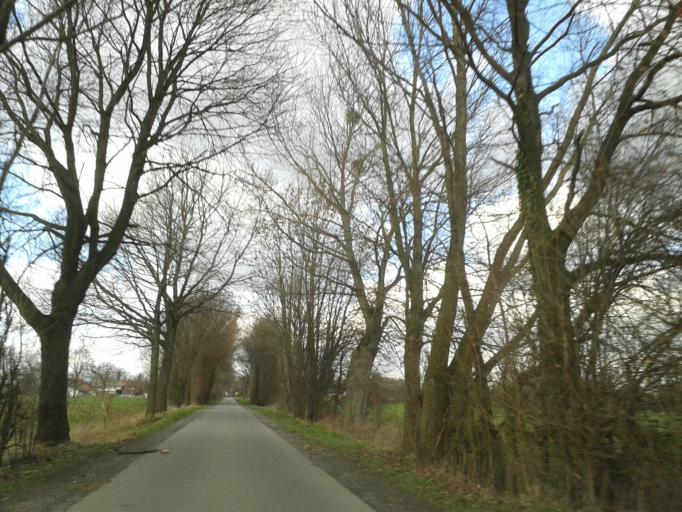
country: DE
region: North Rhine-Westphalia
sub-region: Regierungsbezirk Detmold
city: Salzkotten
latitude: 51.7318
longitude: 8.6326
